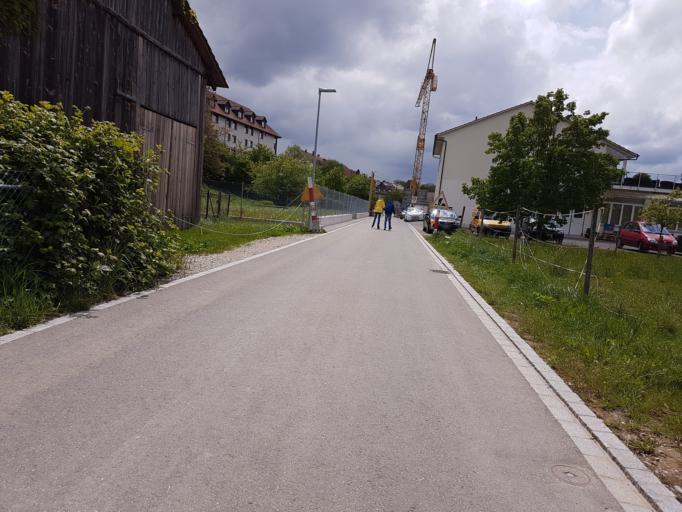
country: CH
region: Aargau
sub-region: Bezirk Zurzach
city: Klingnau
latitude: 47.5728
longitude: 8.2550
